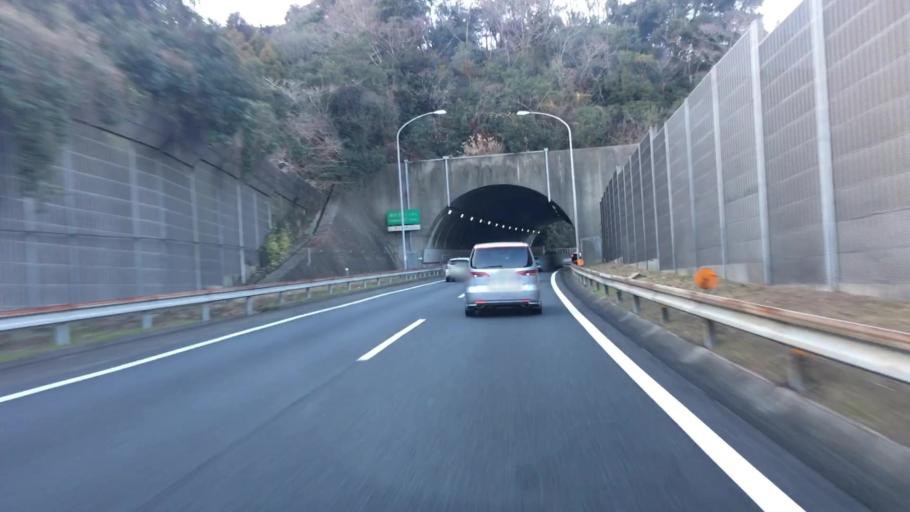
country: JP
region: Kanagawa
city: Zushi
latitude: 35.3267
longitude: 139.5965
